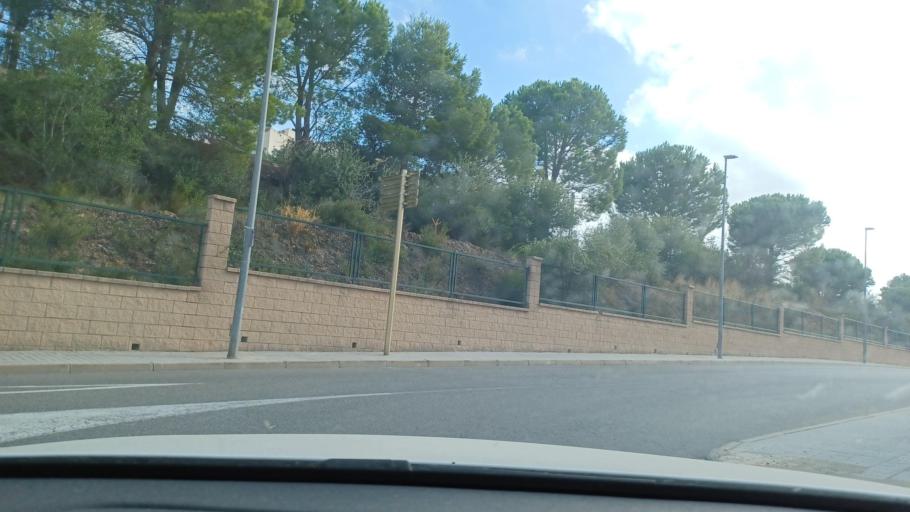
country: ES
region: Catalonia
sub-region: Provincia de Tarragona
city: L'Ampolla
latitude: 40.8141
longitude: 0.7111
